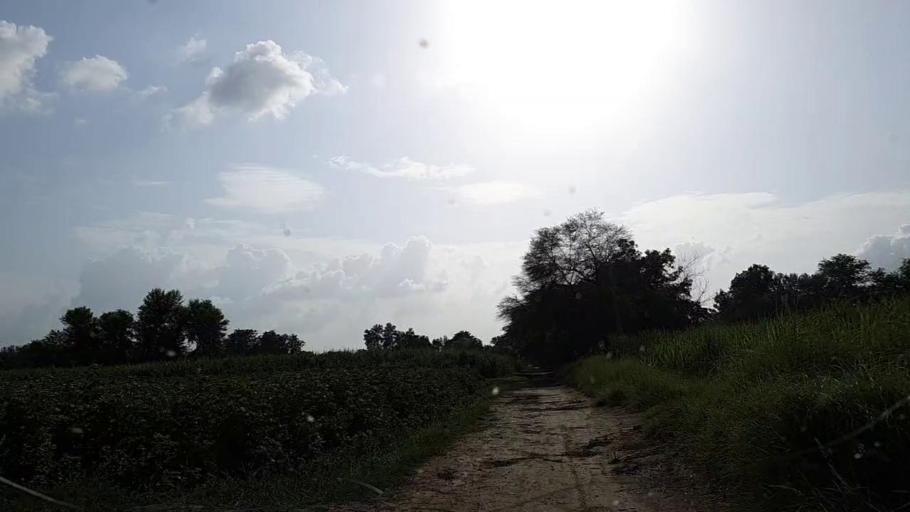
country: PK
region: Sindh
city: Bhiria
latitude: 26.8575
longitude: 68.2484
